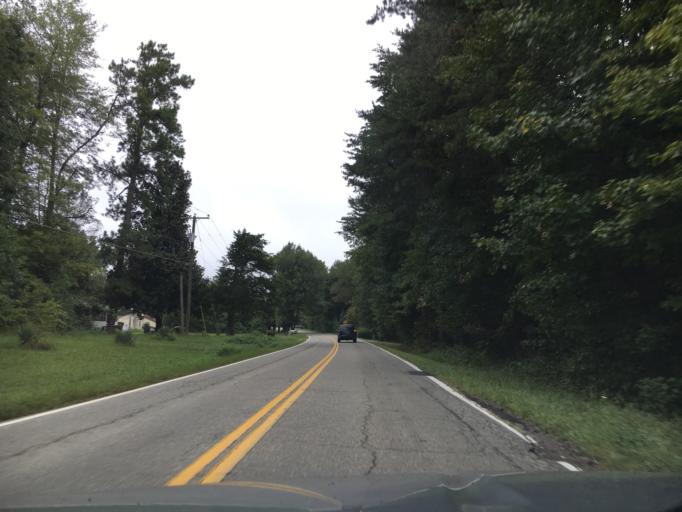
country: US
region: Virginia
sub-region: Powhatan County
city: Powhatan
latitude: 37.4884
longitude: -77.8034
